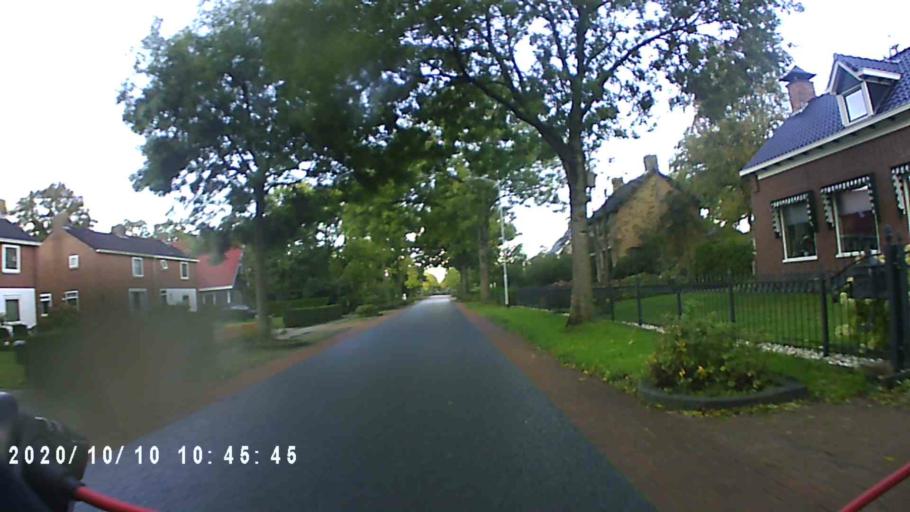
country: NL
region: Groningen
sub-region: Gemeente Grootegast
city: Grootegast
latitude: 53.1697
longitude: 6.2559
